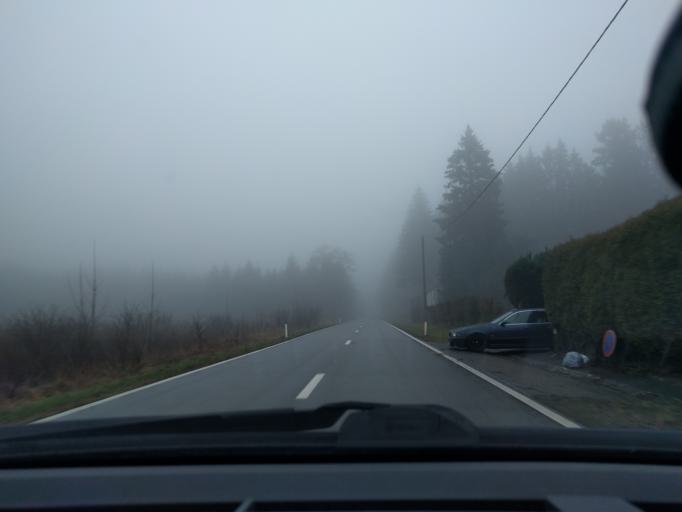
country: BE
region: Wallonia
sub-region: Province du Luxembourg
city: Gouvy
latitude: 50.2036
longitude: 5.9691
